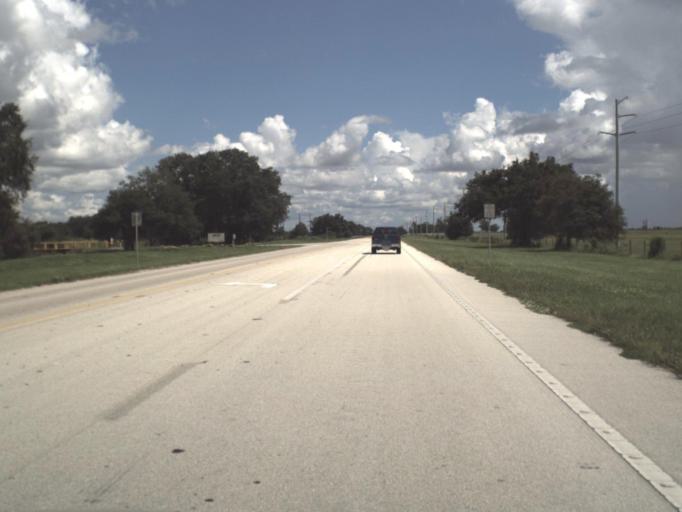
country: US
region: Florida
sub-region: DeSoto County
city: Southeast Arcadia
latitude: 27.2096
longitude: -81.6347
